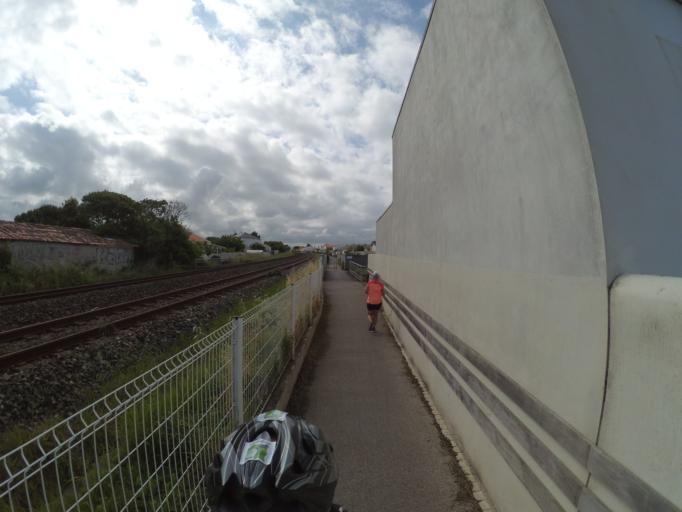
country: FR
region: Poitou-Charentes
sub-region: Departement de la Charente-Maritime
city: Angoulins
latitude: 46.1024
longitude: -1.1128
